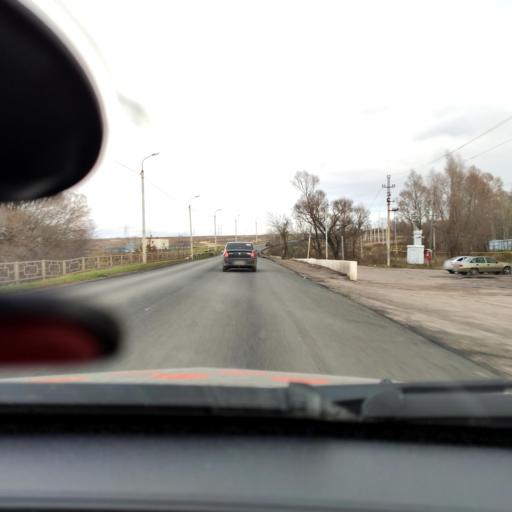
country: RU
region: Bashkortostan
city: Kabakovo
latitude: 54.6403
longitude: 56.0884
